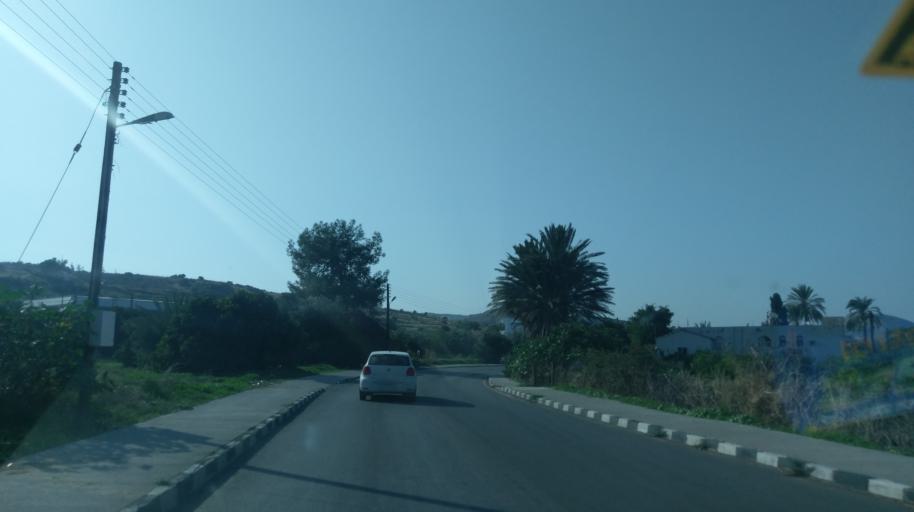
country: CY
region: Lefkosia
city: Lefka
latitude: 35.1417
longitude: 32.8162
